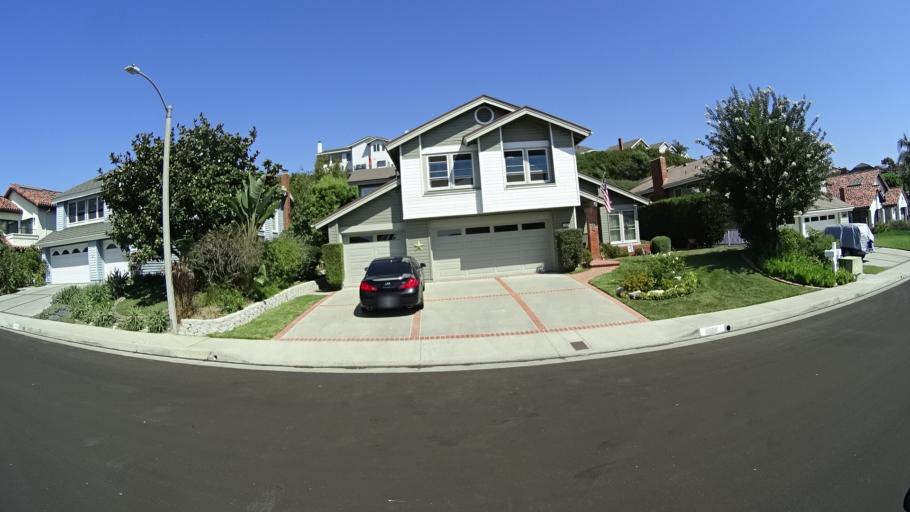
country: US
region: California
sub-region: Orange County
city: San Clemente
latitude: 33.4516
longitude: -117.6377
